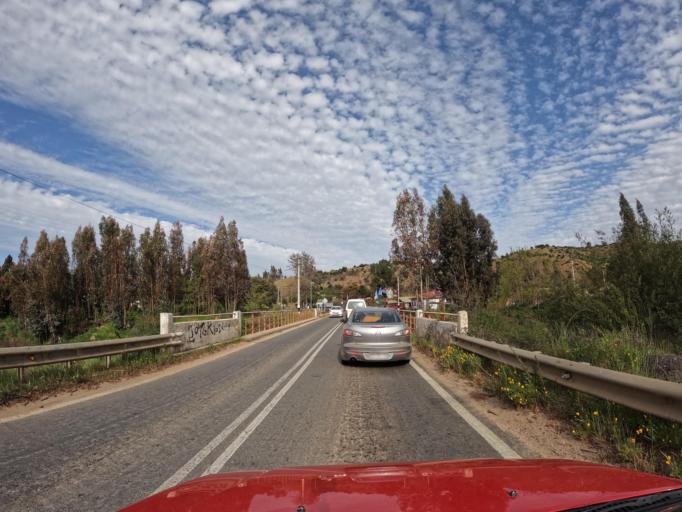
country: CL
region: O'Higgins
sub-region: Provincia de Colchagua
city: Santa Cruz
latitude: -34.3018
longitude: -71.7959
